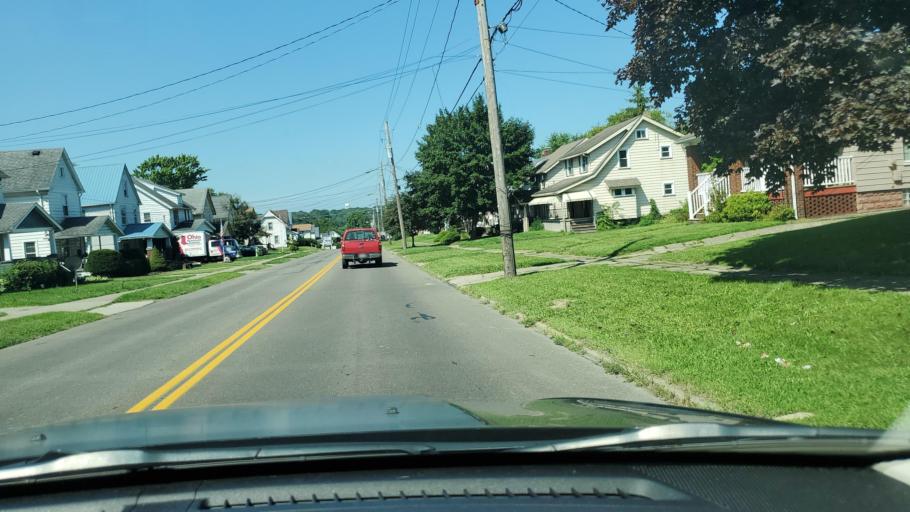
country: US
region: Ohio
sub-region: Trumbull County
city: Girard
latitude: 41.1620
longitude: -80.6995
